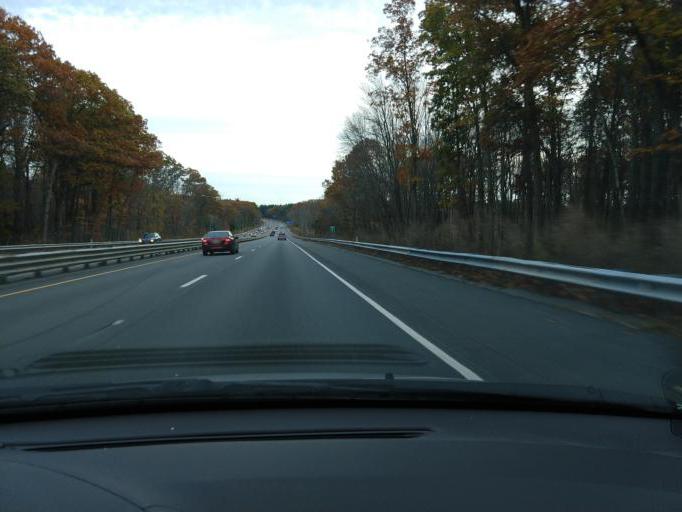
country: US
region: Massachusetts
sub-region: Middlesex County
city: Littleton Common
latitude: 42.5117
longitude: -71.4921
